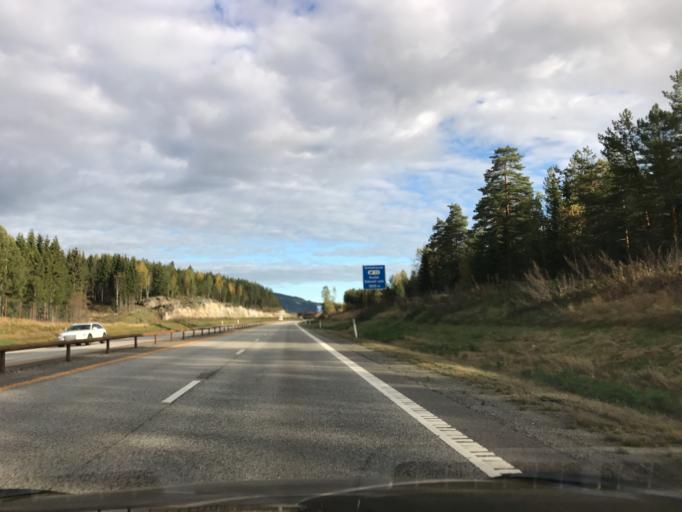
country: NO
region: Akershus
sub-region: Eidsvoll
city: Raholt
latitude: 60.2984
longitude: 11.1382
